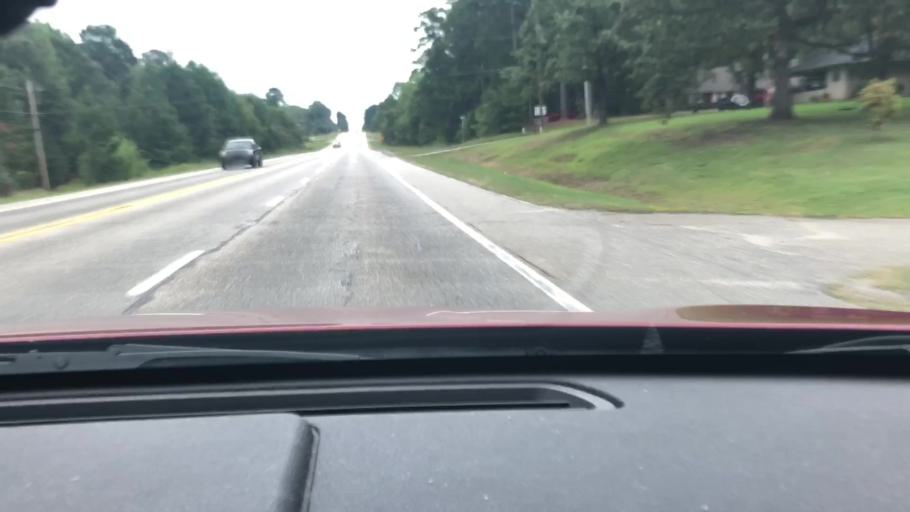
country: US
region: Arkansas
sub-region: Miller County
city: Texarkana
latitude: 33.4295
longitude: -93.9472
